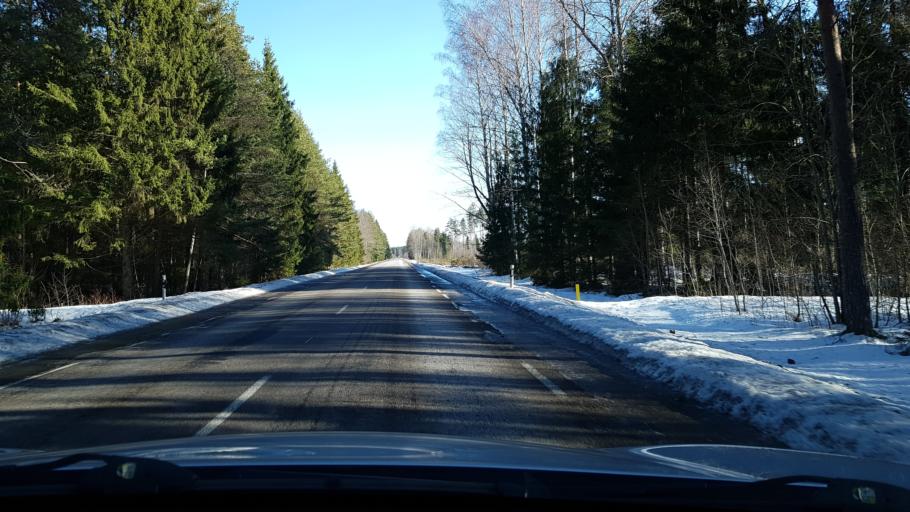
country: EE
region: Viljandimaa
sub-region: Suure-Jaani vald
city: Suure-Jaani
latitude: 58.5799
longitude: 25.2561
